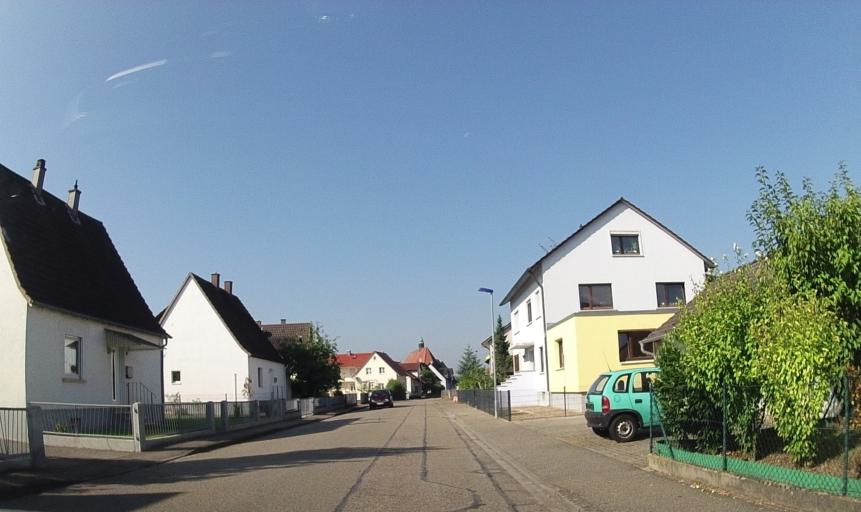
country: DE
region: Baden-Wuerttemberg
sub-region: Karlsruhe Region
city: Durmersheim
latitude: 48.9387
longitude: 8.2763
